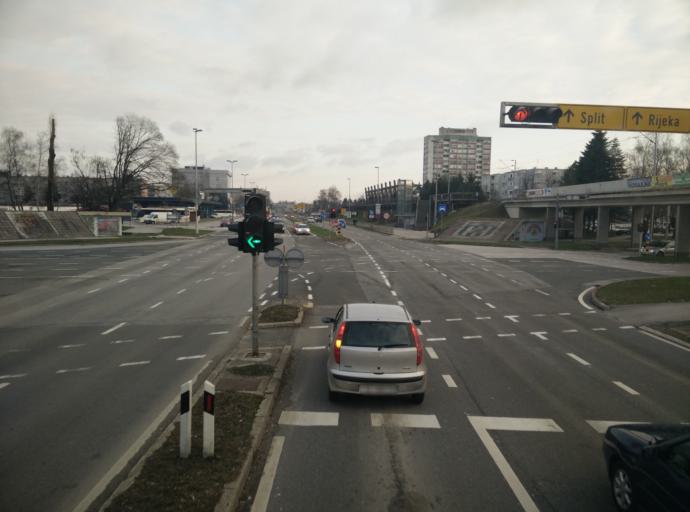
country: HR
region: Karlovacka
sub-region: Grad Karlovac
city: Karlovac
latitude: 45.4896
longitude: 15.5484
